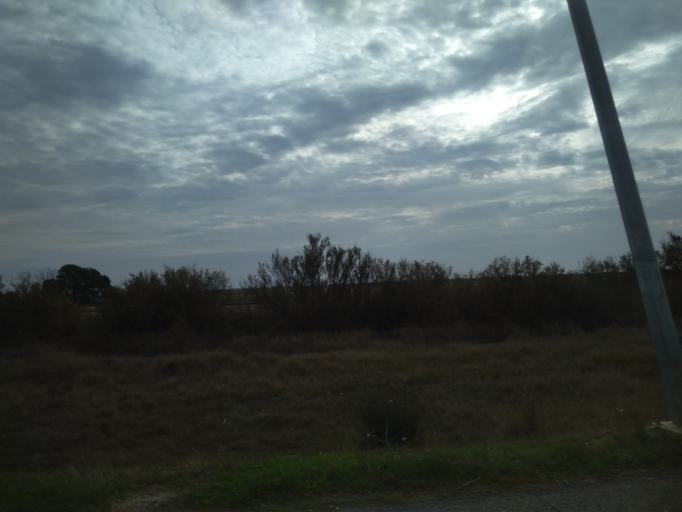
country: PT
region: Faro
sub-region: Olhao
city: Olhao
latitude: 37.0278
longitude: -7.8773
